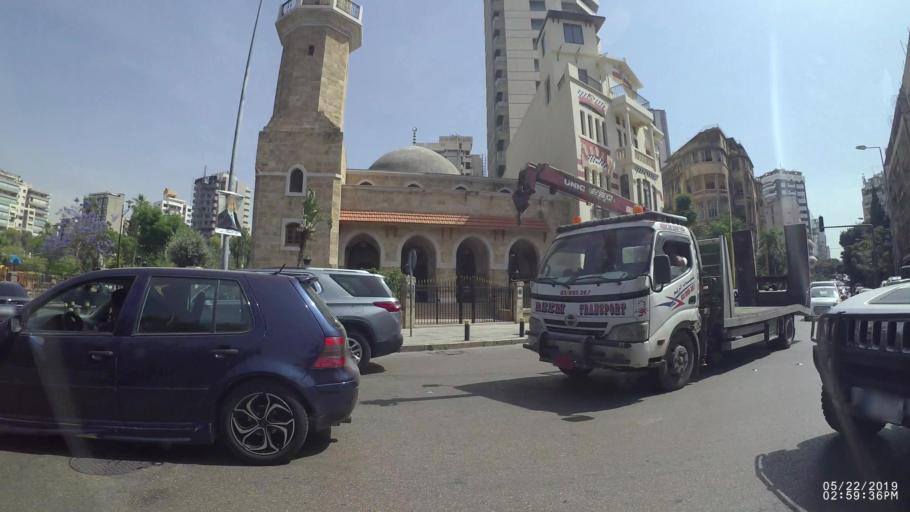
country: LB
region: Beyrouth
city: Beirut
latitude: 33.8944
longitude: 35.4890
